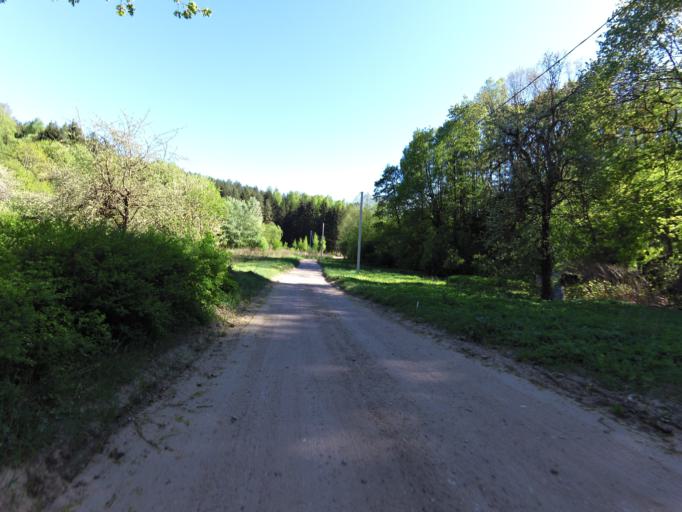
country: LT
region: Vilnius County
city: Pilaite
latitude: 54.6895
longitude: 25.1551
